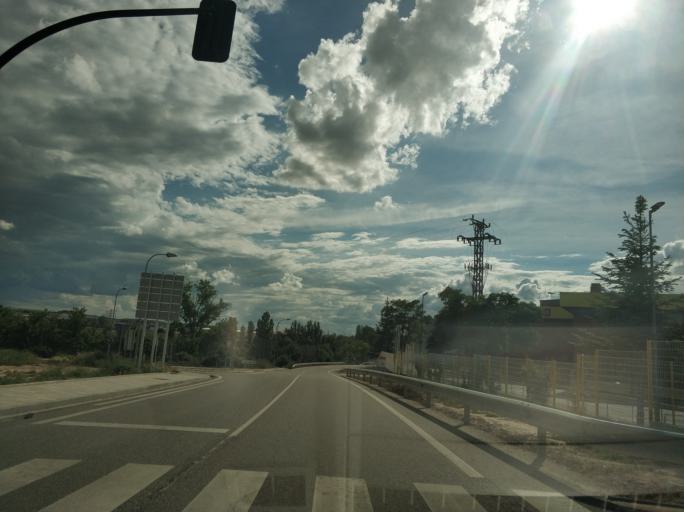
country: ES
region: Castille and Leon
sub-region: Provincia de Burgos
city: Aranda de Duero
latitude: 41.6758
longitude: -3.6986
